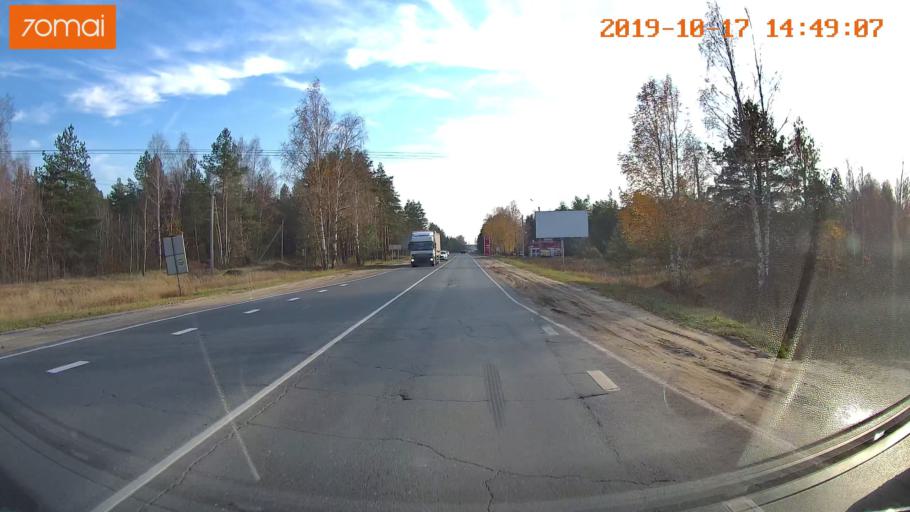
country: RU
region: Rjazan
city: Polyany
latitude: 54.7511
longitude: 39.8389
